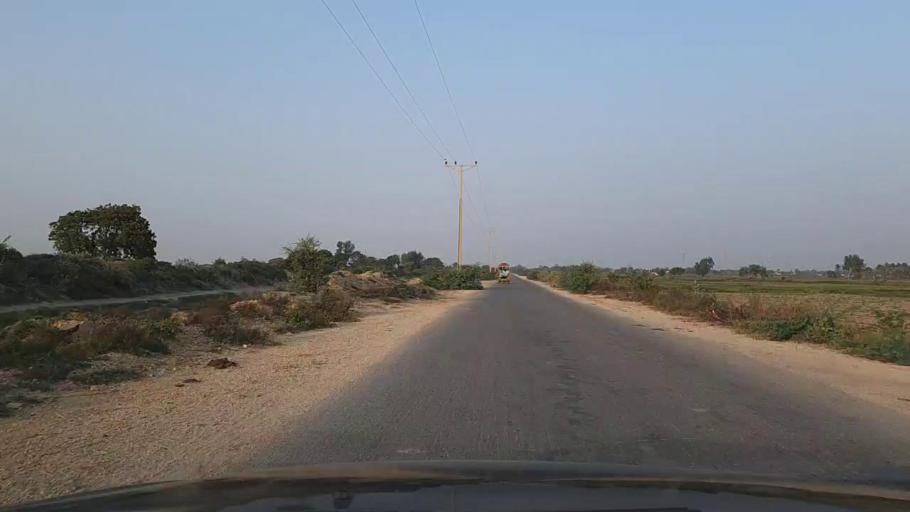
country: PK
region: Sindh
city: Mirpur Sakro
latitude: 24.5401
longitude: 67.8332
